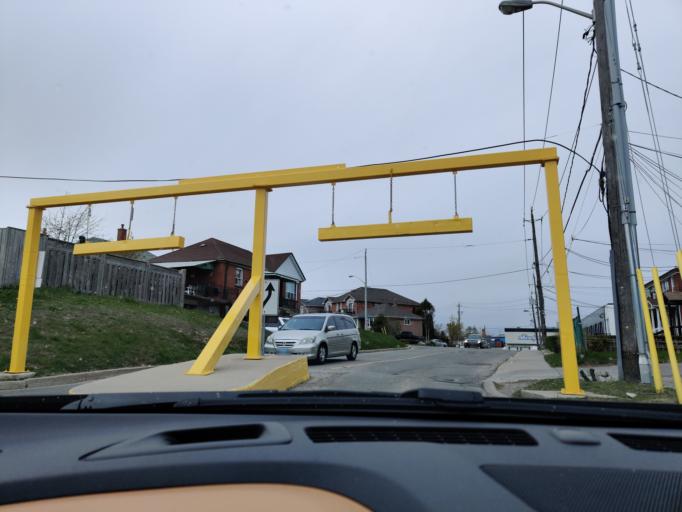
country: CA
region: Ontario
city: Toronto
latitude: 43.6941
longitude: -79.4662
